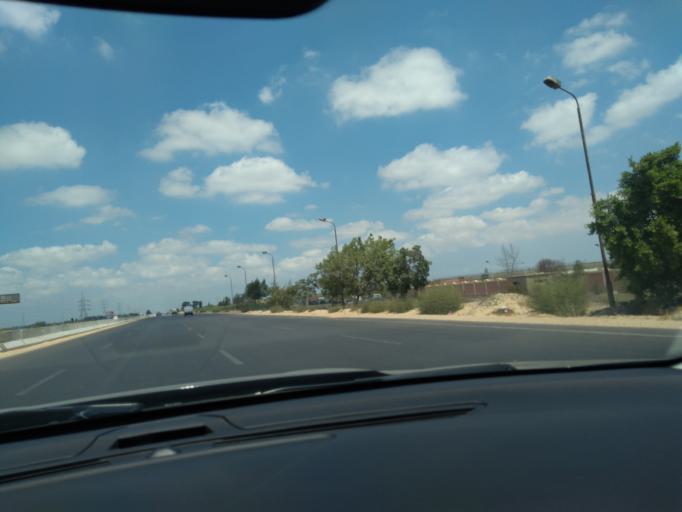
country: EG
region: Muhafazat Bur Sa`id
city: Port Said
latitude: 31.0196
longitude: 32.3066
